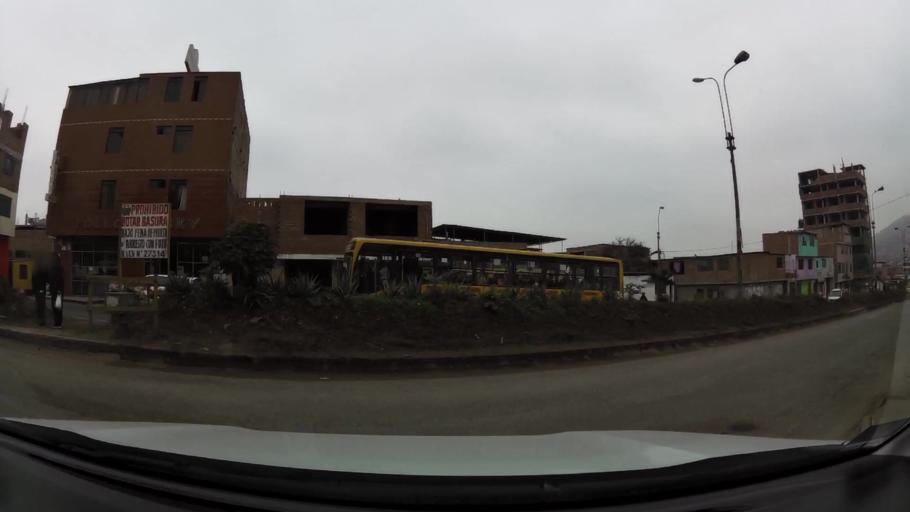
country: PE
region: Lima
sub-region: Lima
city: Surco
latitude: -12.1673
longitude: -76.9610
